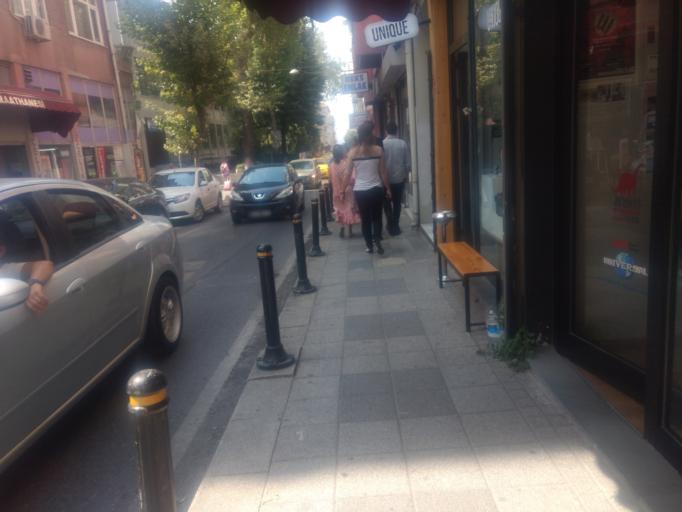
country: TR
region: Istanbul
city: UEskuedar
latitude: 40.9853
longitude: 29.0245
